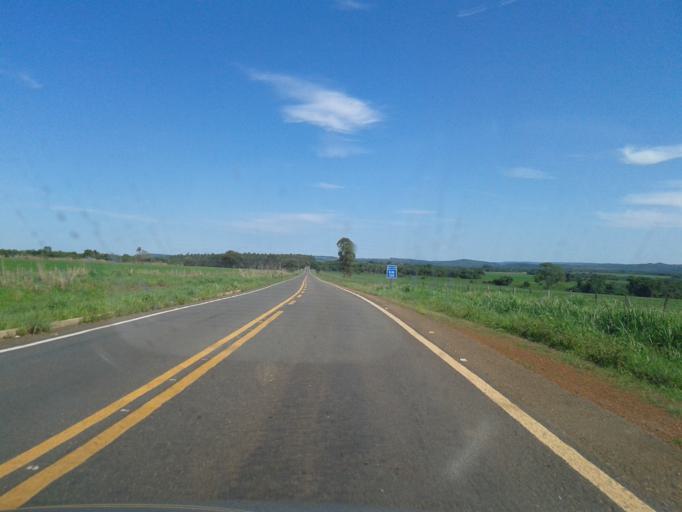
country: BR
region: Goias
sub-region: Piracanjuba
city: Piracanjuba
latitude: -17.3403
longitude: -48.7934
